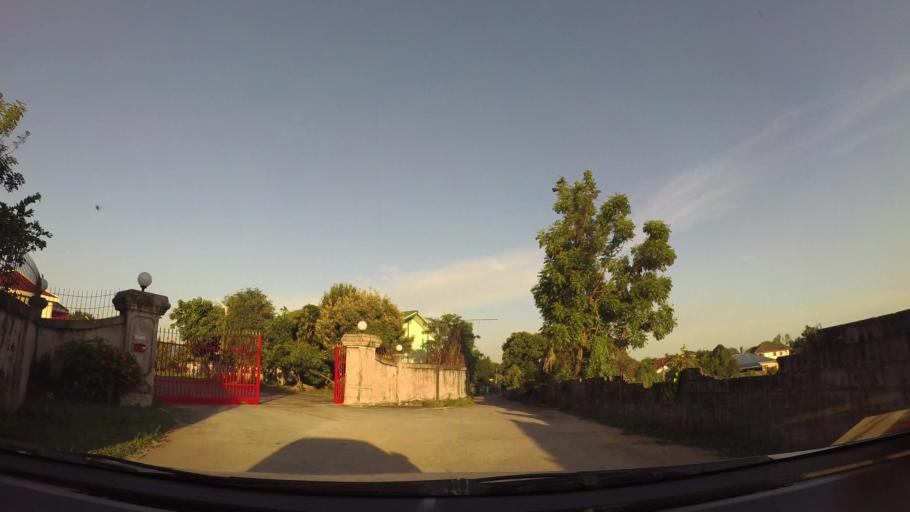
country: TH
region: Chon Buri
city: Si Racha
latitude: 13.1321
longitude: 100.9380
